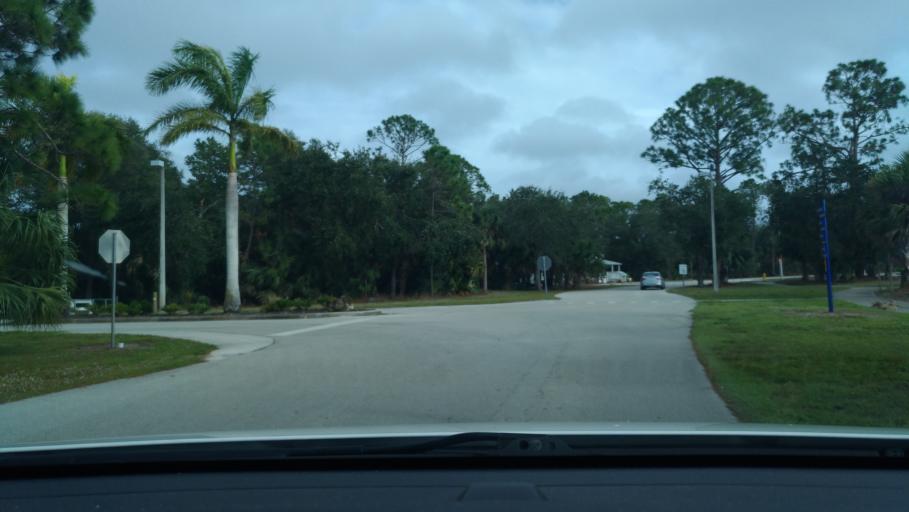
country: US
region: Florida
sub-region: Lee County
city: Estero
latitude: 26.4294
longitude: -81.8002
